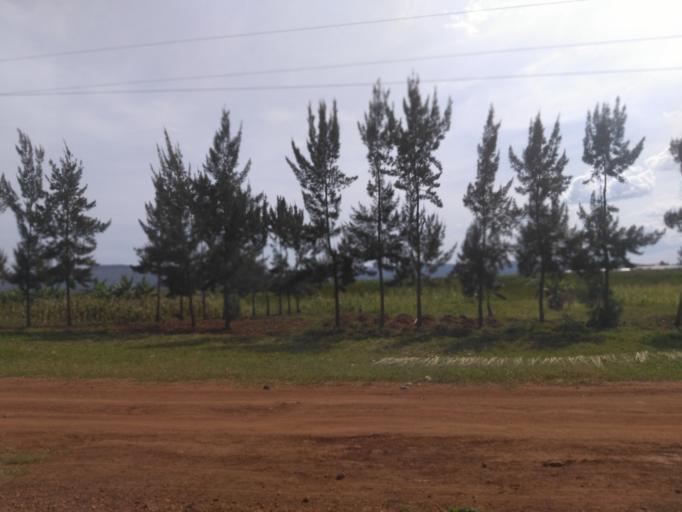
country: UG
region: Eastern Region
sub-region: Jinja District
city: Jinja
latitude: 0.4219
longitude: 33.2246
